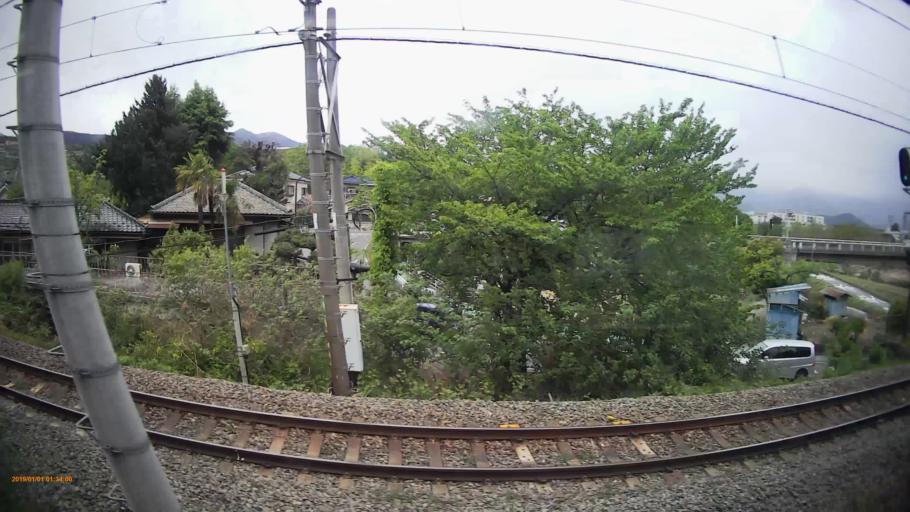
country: JP
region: Yamanashi
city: Enzan
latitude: 35.6861
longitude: 138.6783
